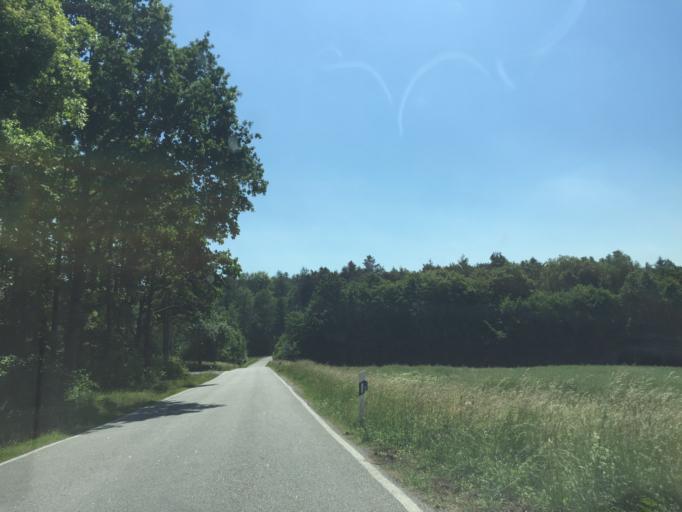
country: DE
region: Baden-Wuerttemberg
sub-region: Karlsruhe Region
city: Walldurn
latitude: 49.6088
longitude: 9.3434
